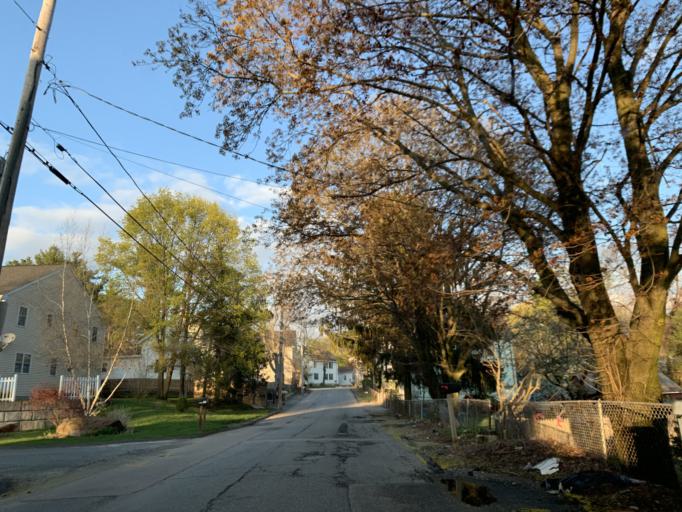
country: US
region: Rhode Island
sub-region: Providence County
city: Valley Falls
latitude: 41.8998
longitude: -71.3814
